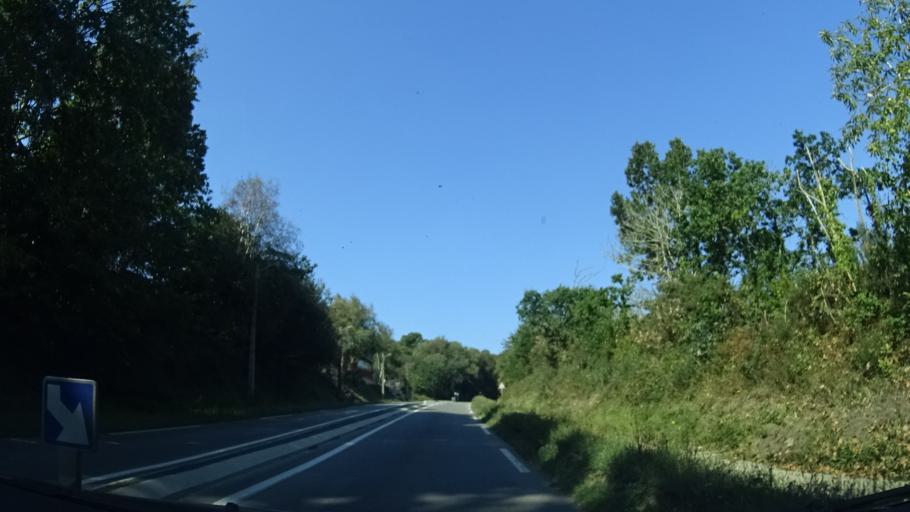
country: FR
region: Brittany
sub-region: Departement du Finistere
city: Douarnenez
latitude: 48.0820
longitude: -4.3316
